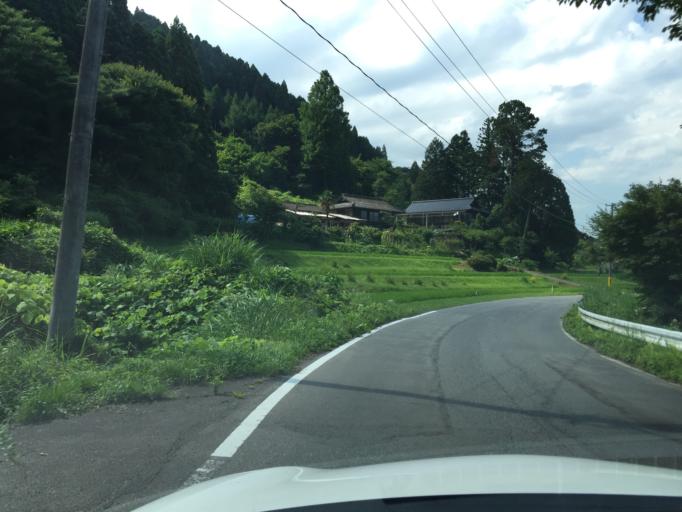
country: JP
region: Ibaraki
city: Kitaibaraki
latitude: 36.9747
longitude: 140.7032
